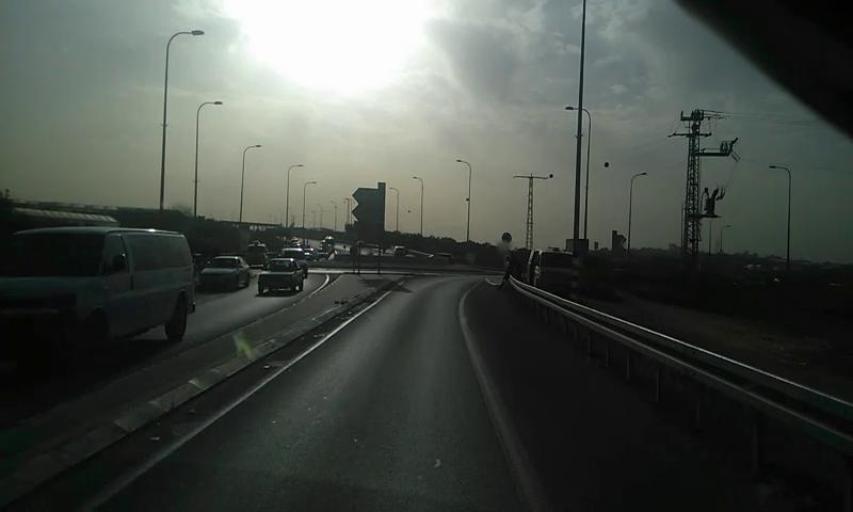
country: PS
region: West Bank
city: An Nabi Ilyas
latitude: 32.1866
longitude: 35.0028
